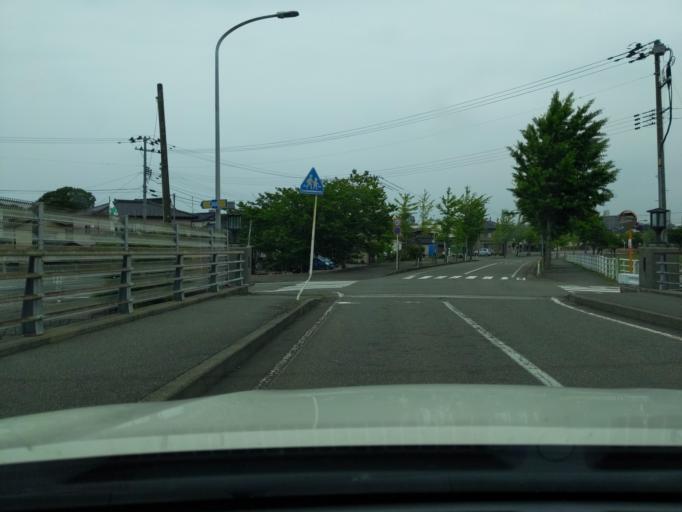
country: JP
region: Niigata
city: Kashiwazaki
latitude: 37.3644
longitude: 138.5463
